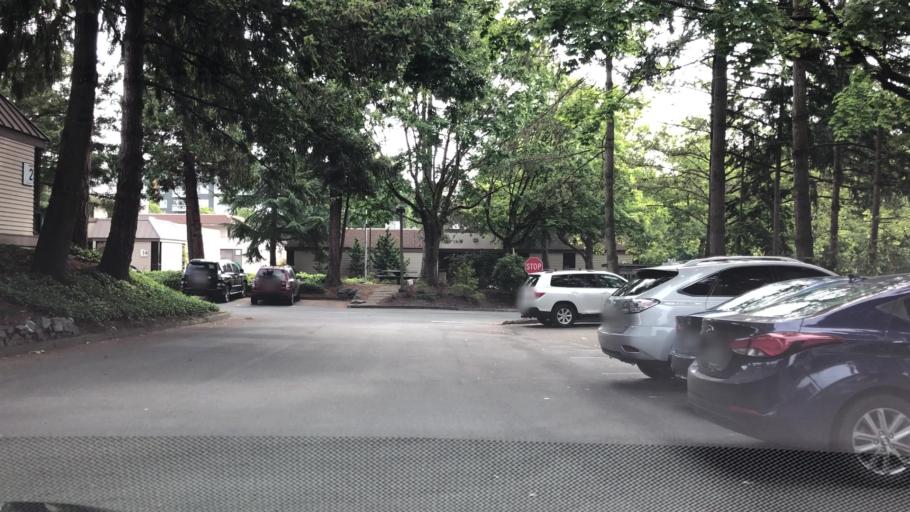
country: US
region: Washington
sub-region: King County
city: Redmond
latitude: 47.6332
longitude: -122.1400
